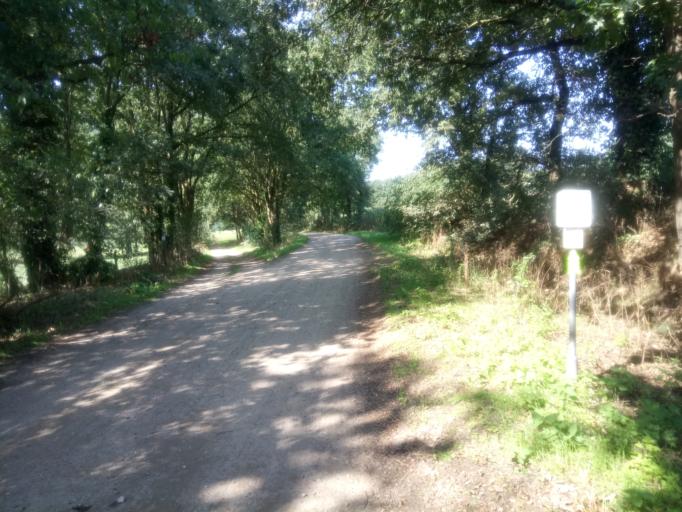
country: BE
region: Flanders
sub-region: Provincie Antwerpen
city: Meerhout
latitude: 51.1344
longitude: 5.0442
